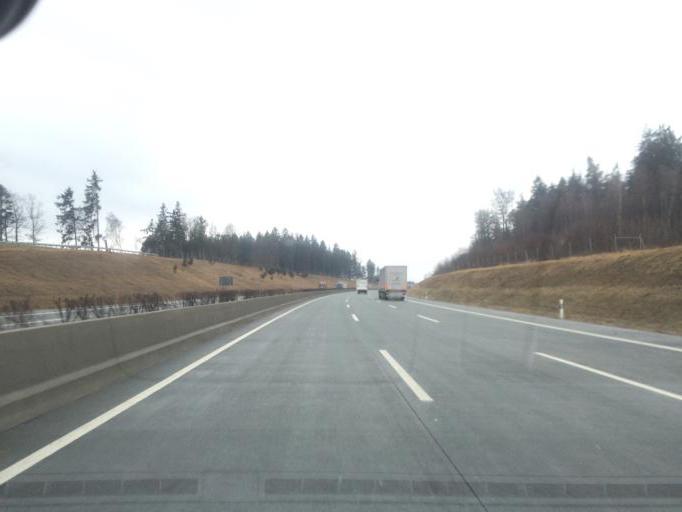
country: DE
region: Thuringia
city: Tommelsdorf
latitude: 50.7106
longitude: 11.8525
